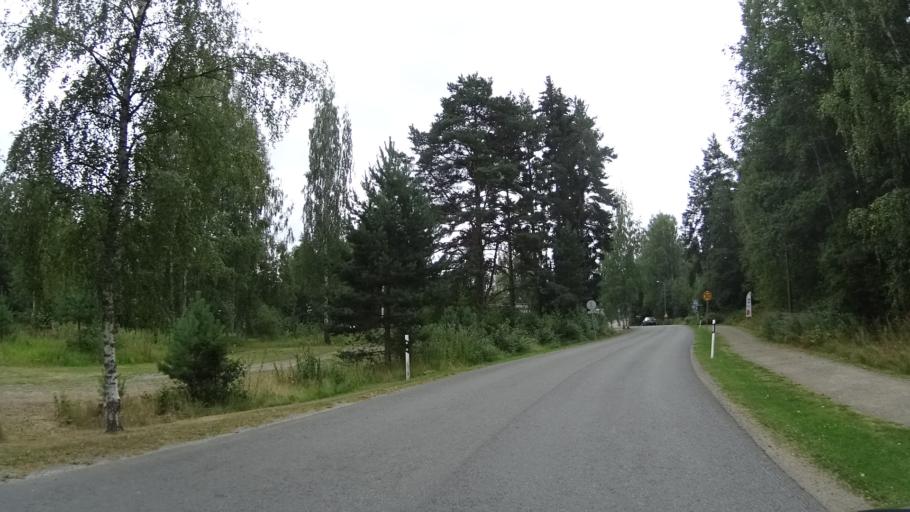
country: FI
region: Pirkanmaa
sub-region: Tampere
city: Kangasala
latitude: 61.4426
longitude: 24.1297
